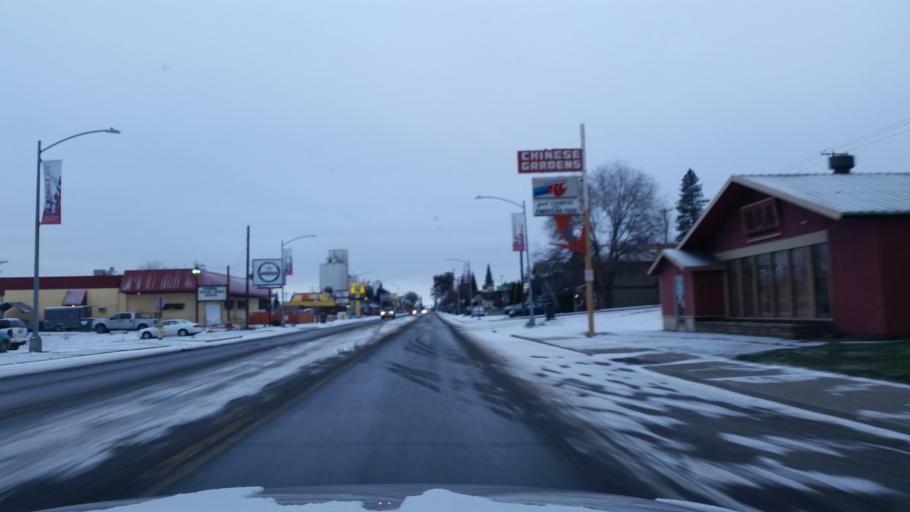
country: US
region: Washington
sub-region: Spokane County
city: Cheney
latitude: 47.4921
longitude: -117.5697
